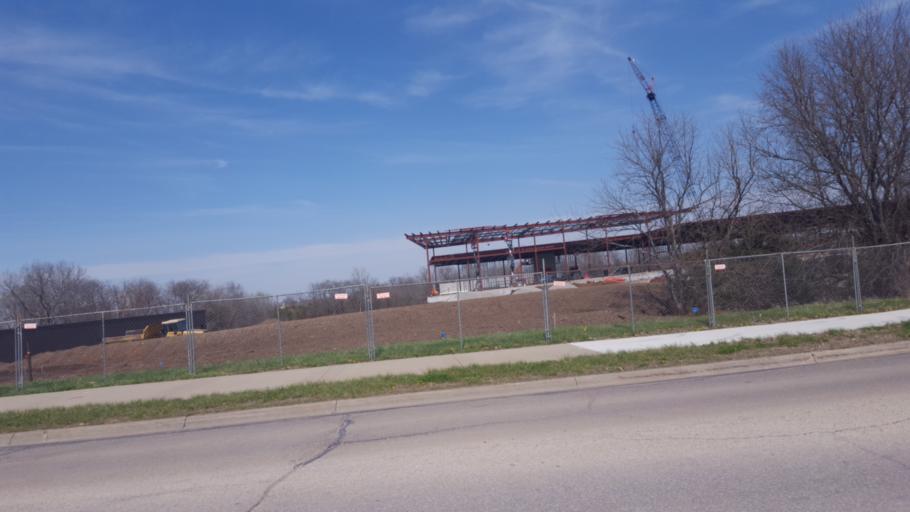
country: US
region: Kansas
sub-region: Douglas County
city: Lawrence
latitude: 38.9748
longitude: -95.3115
